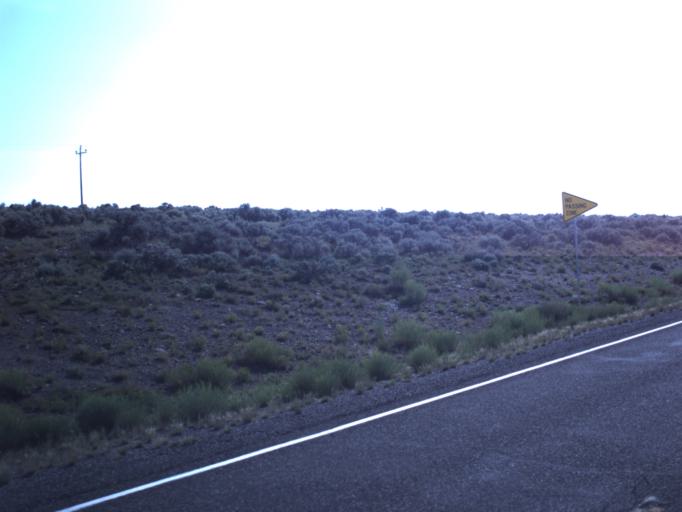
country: US
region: Utah
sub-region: Wayne County
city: Loa
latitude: 38.4480
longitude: -111.8131
